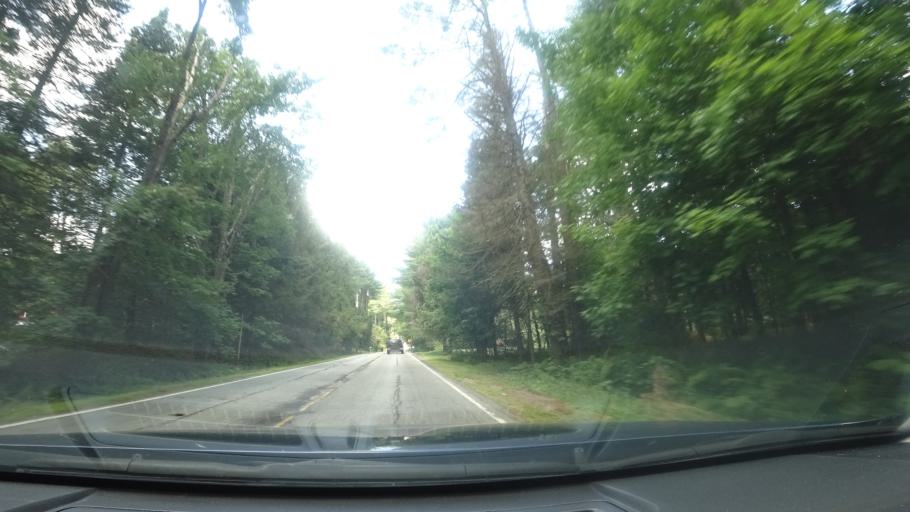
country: US
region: New York
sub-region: Warren County
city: Warrensburg
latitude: 43.6603
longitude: -73.8344
